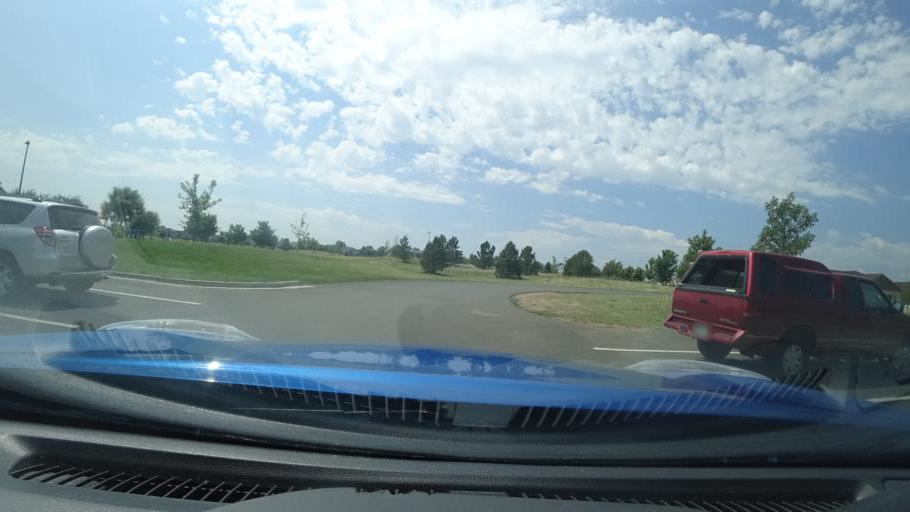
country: US
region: Colorado
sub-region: Adams County
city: Aurora
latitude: 39.6805
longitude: -104.7564
